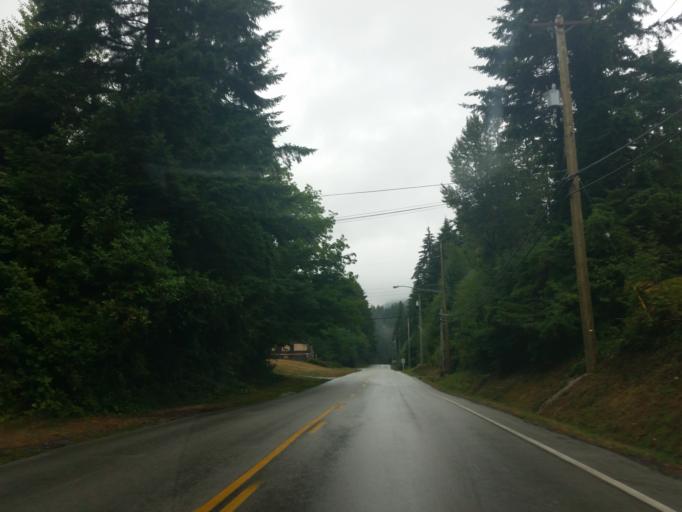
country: CA
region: British Columbia
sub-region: Greater Vancouver Regional District
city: Anmore
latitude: 49.3037
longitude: -122.8735
